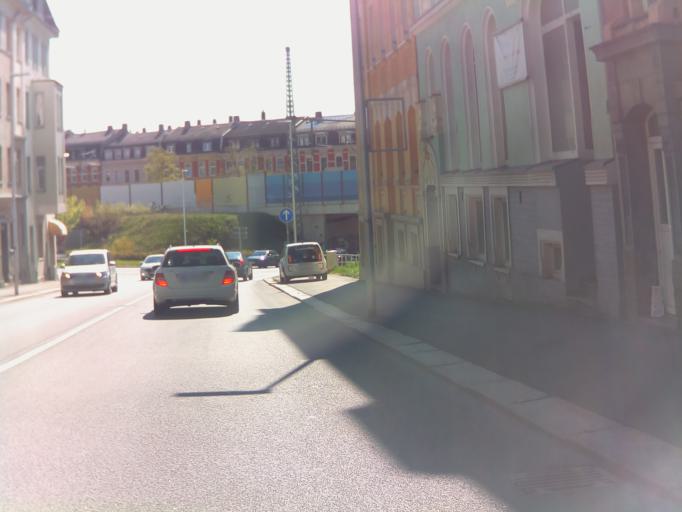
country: DE
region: Saxony
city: Plauen
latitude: 50.5073
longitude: 12.1350
